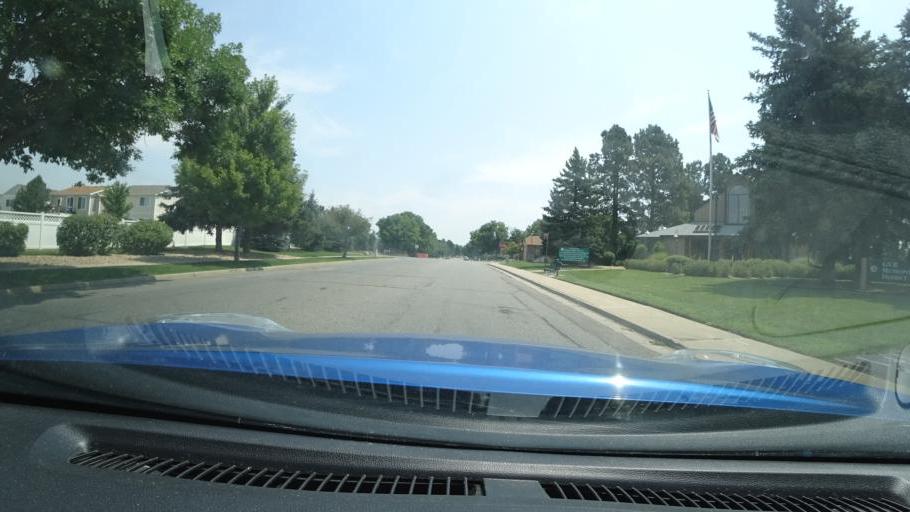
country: US
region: Colorado
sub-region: Adams County
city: Aurora
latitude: 39.7780
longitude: -104.7699
